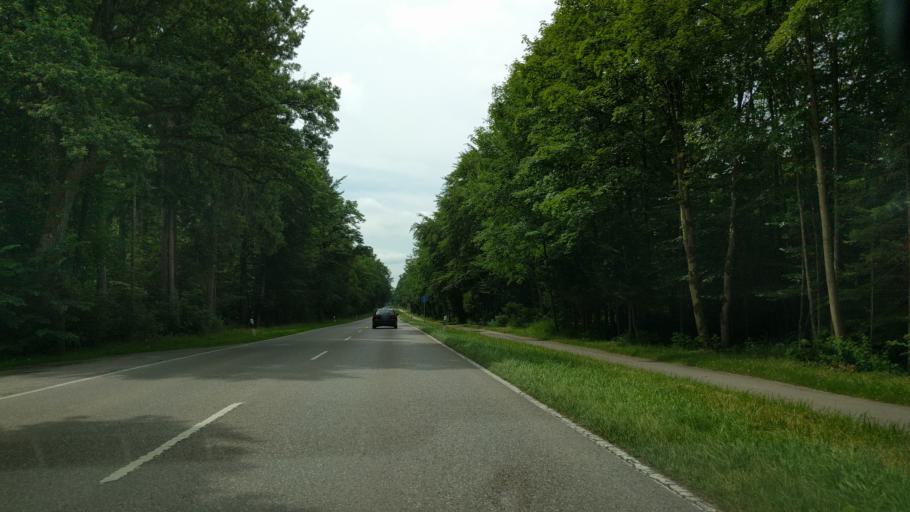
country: DE
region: Bavaria
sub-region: Upper Bavaria
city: Strasslach-Dingharting
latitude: 48.0209
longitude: 11.5176
